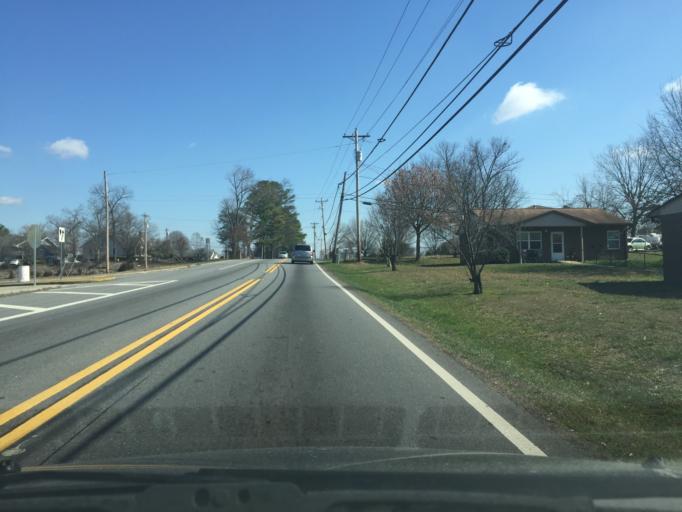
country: US
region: Georgia
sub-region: Catoosa County
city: Fort Oglethorpe
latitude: 34.9570
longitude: -85.2361
